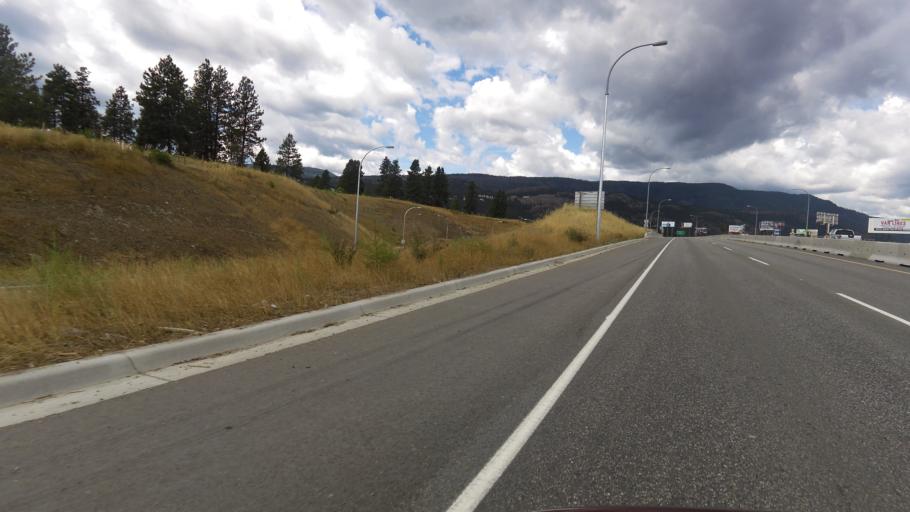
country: CA
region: British Columbia
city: Kelowna
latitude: 49.8833
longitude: -119.5258
